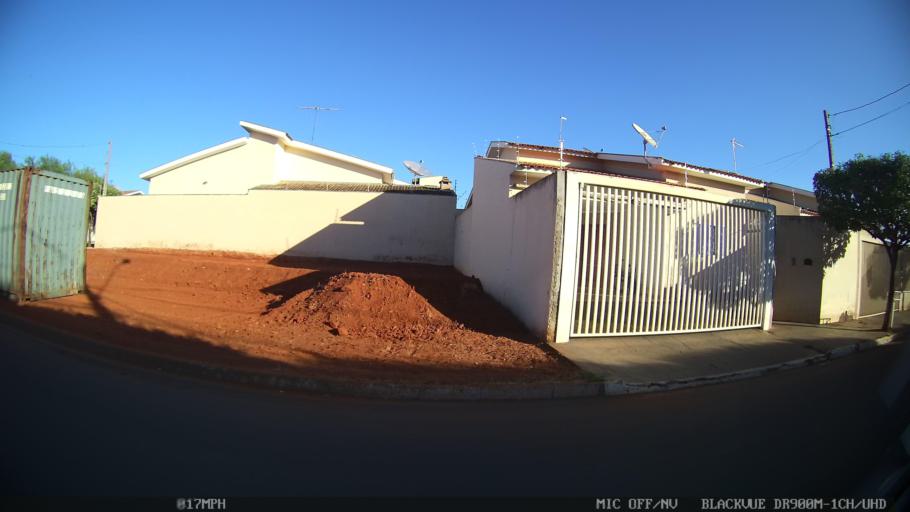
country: BR
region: Sao Paulo
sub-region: Guapiacu
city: Guapiacu
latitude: -20.7947
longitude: -49.2280
